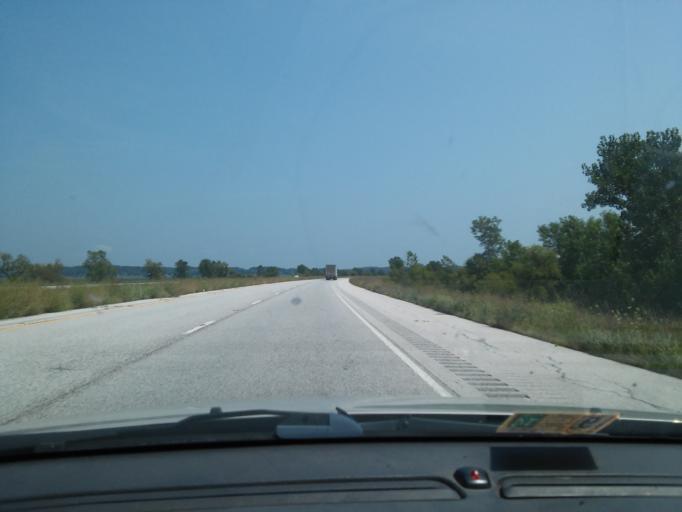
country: US
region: Illinois
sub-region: Pike County
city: Griggsville
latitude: 39.6916
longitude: -90.6103
